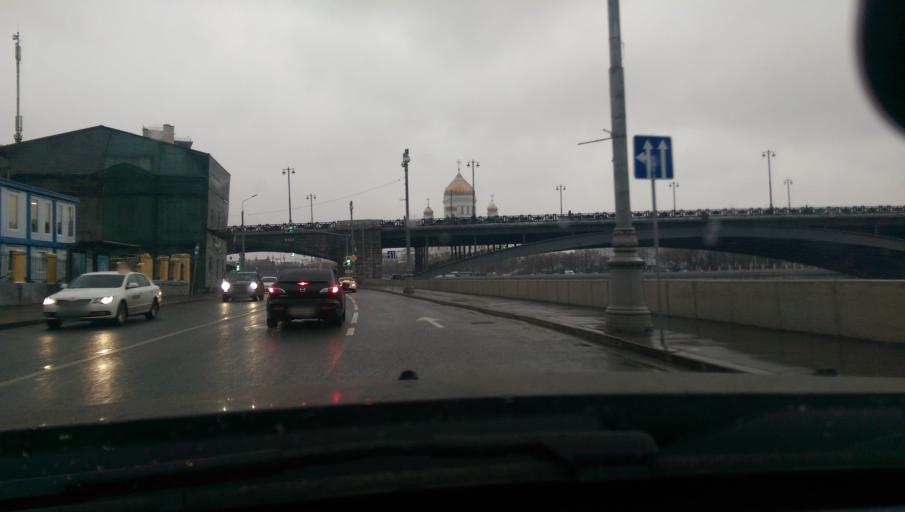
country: RU
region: Moscow
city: Moscow
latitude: 55.7469
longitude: 37.6142
